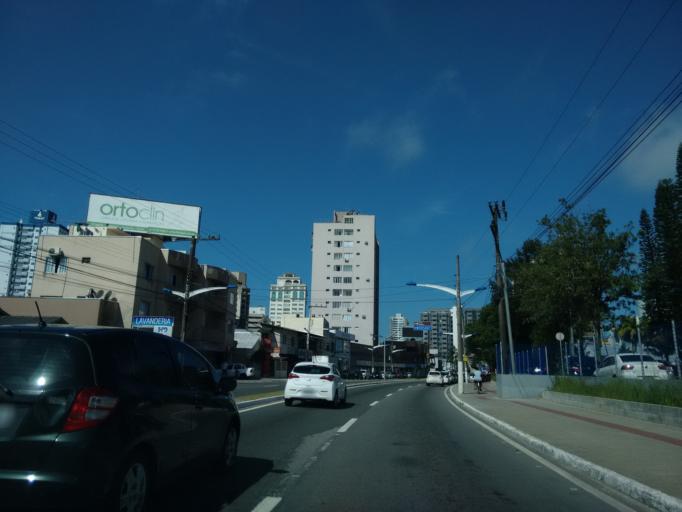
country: BR
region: Santa Catarina
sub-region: Itajai
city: Itajai
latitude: -26.9140
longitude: -48.6624
